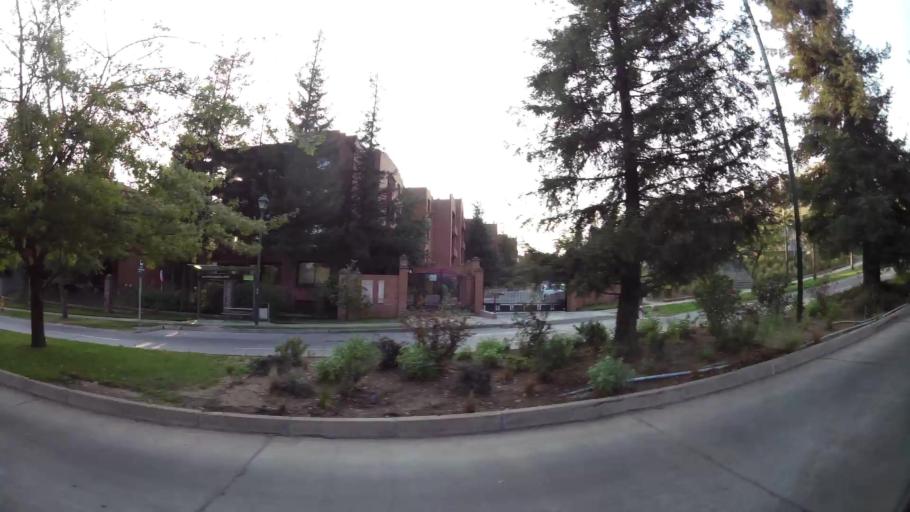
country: CL
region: Santiago Metropolitan
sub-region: Provincia de Santiago
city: Villa Presidente Frei, Nunoa, Santiago, Chile
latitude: -33.3354
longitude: -70.5077
